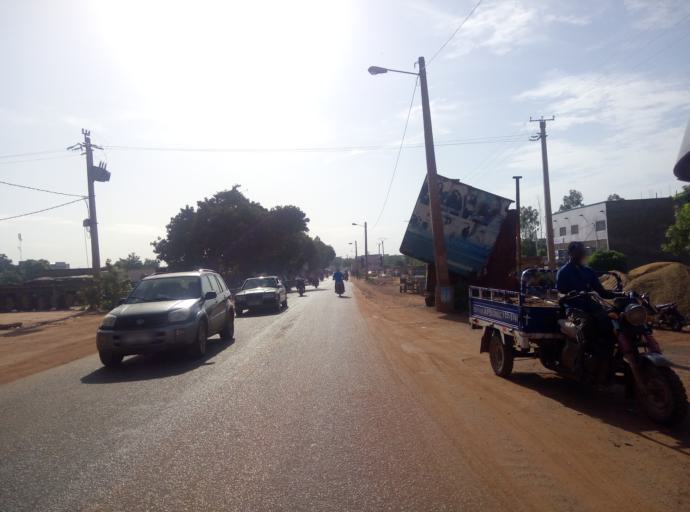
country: ML
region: Bamako
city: Bamako
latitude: 12.6532
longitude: -7.9388
